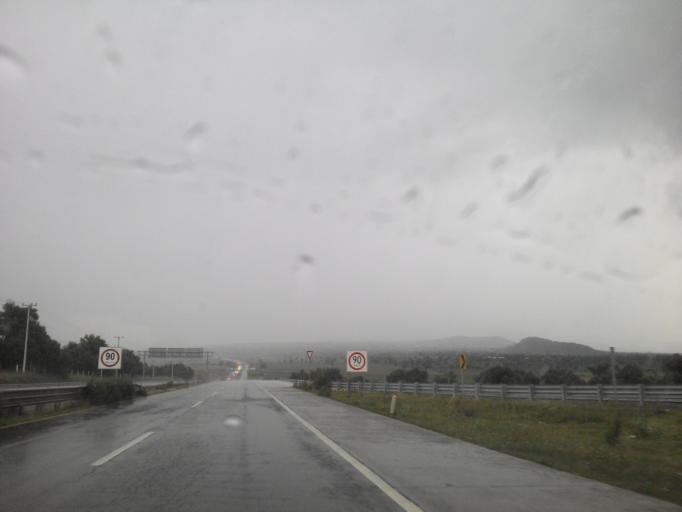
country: MX
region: Morelos
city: Nopaltepec
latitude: 19.8347
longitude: -98.6989
